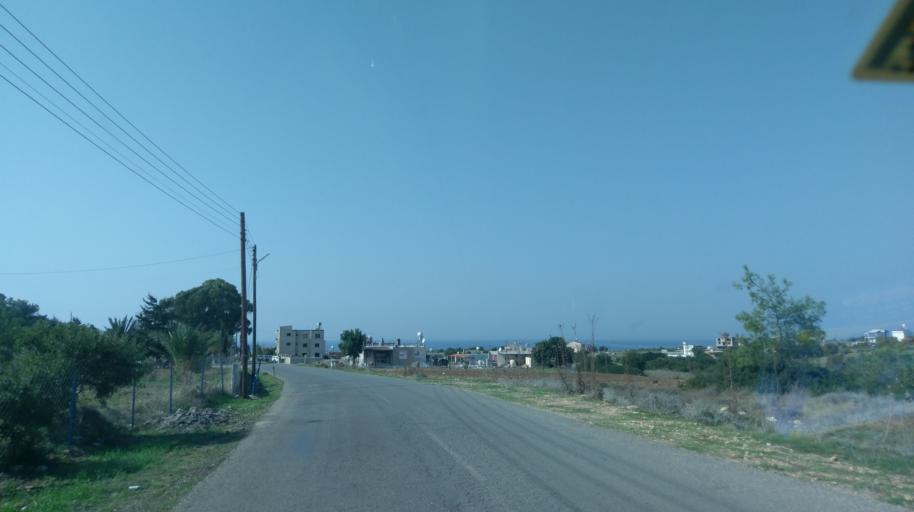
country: CY
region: Lefkosia
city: Morfou
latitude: 35.2989
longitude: 32.9690
